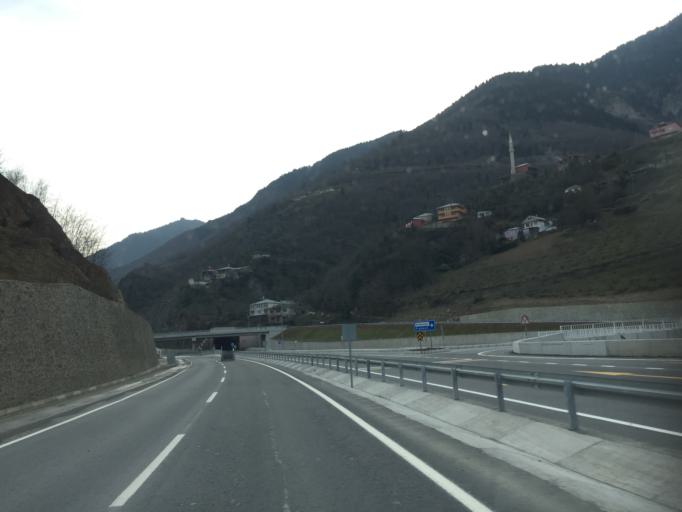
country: TR
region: Trabzon
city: Macka
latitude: 40.7808
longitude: 39.5710
